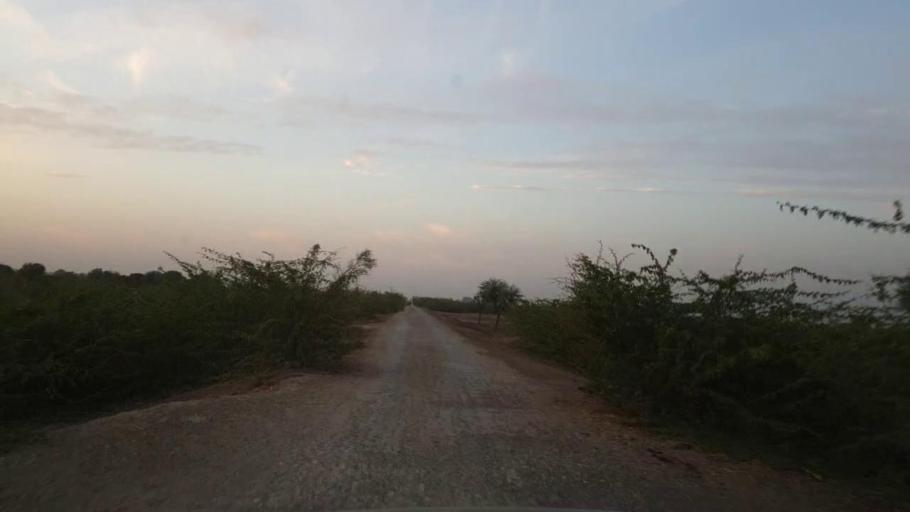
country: PK
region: Sindh
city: Kunri
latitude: 25.1363
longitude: 69.5627
